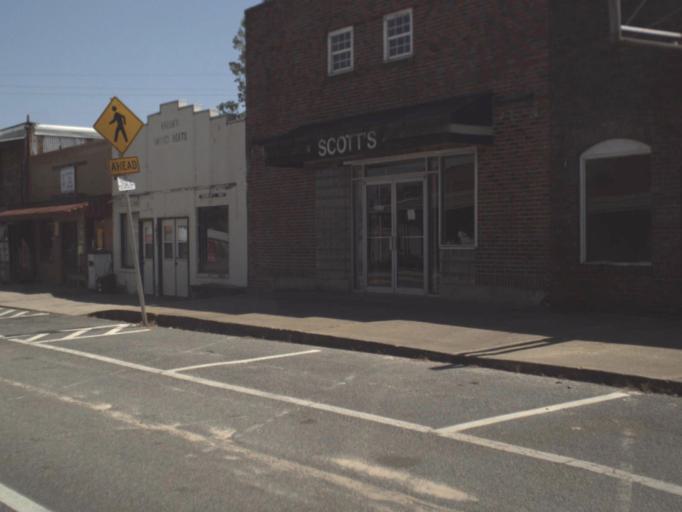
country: US
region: Florida
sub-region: Escambia County
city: Century
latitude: 30.9530
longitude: -87.1511
